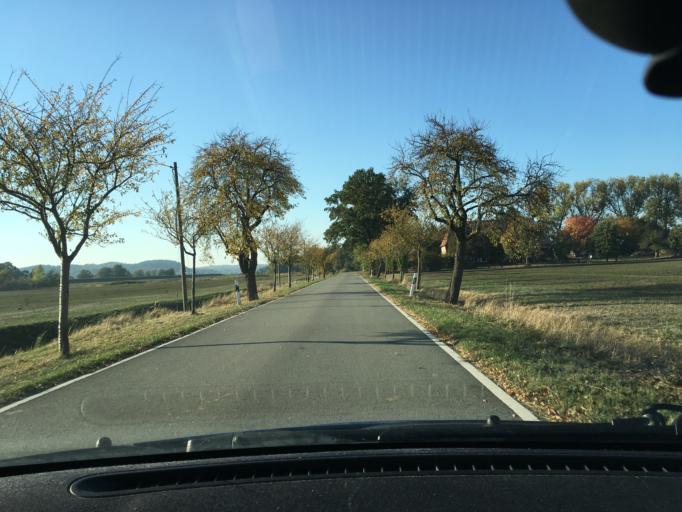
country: DE
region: Lower Saxony
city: Hitzacker
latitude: 53.1893
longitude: 11.0071
